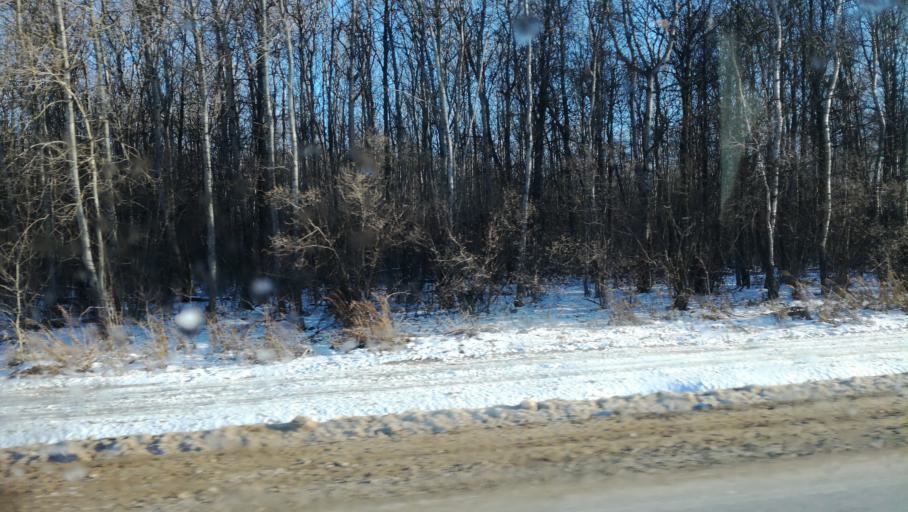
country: RU
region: Tula
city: Barsuki
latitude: 54.1723
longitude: 37.4566
